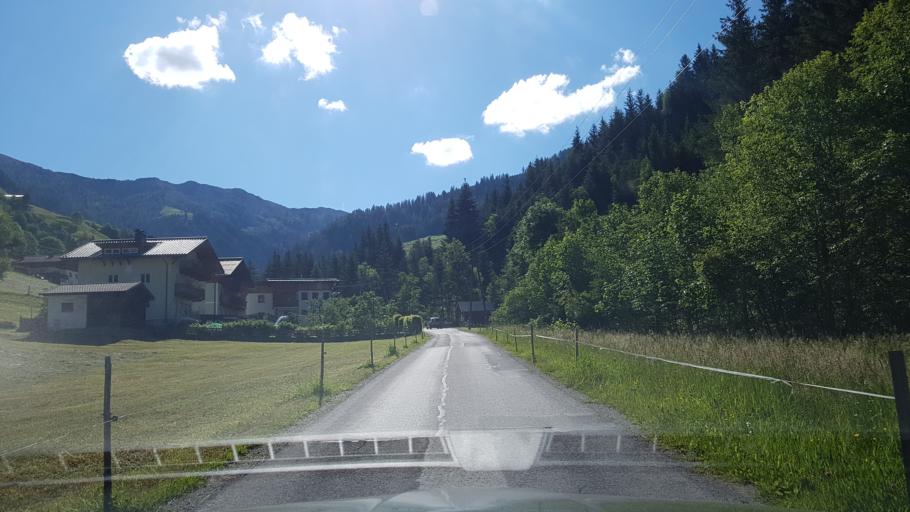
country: AT
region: Salzburg
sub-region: Politischer Bezirk Sankt Johann im Pongau
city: Huttschlag
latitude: 47.2351
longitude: 13.2439
